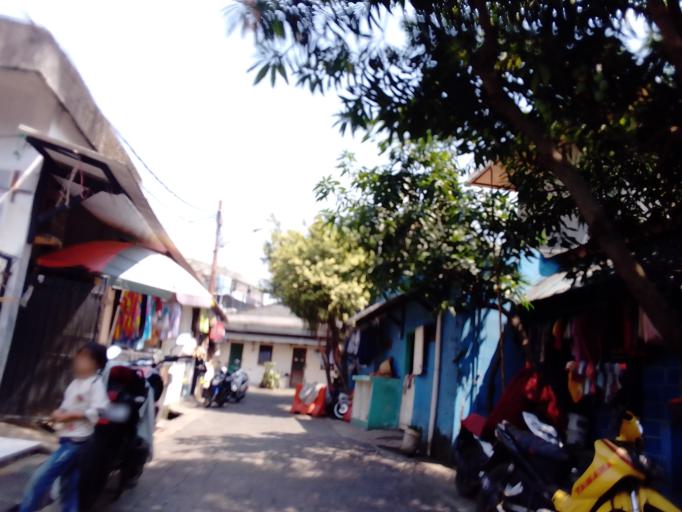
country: ID
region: Jakarta Raya
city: Jakarta
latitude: -6.2607
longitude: 106.8035
